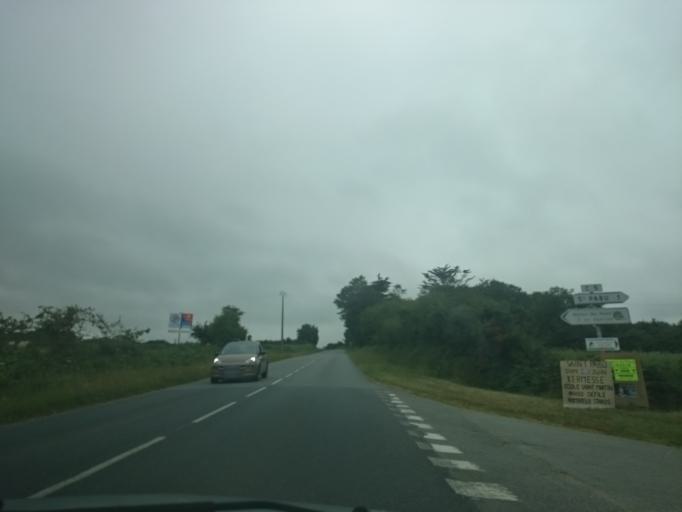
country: FR
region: Brittany
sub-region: Departement du Finistere
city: Saint-Pabu
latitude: 48.5519
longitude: -4.6040
